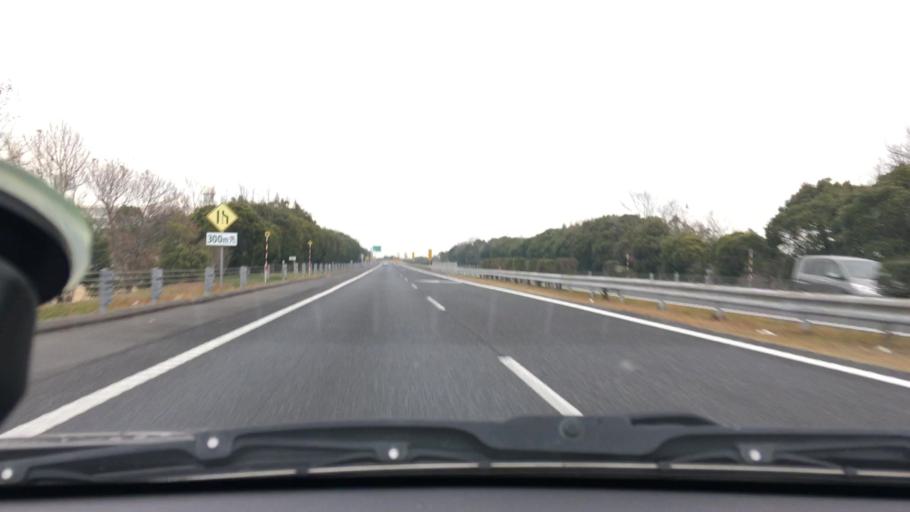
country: JP
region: Ibaraki
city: Itako
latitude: 35.9294
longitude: 140.5857
